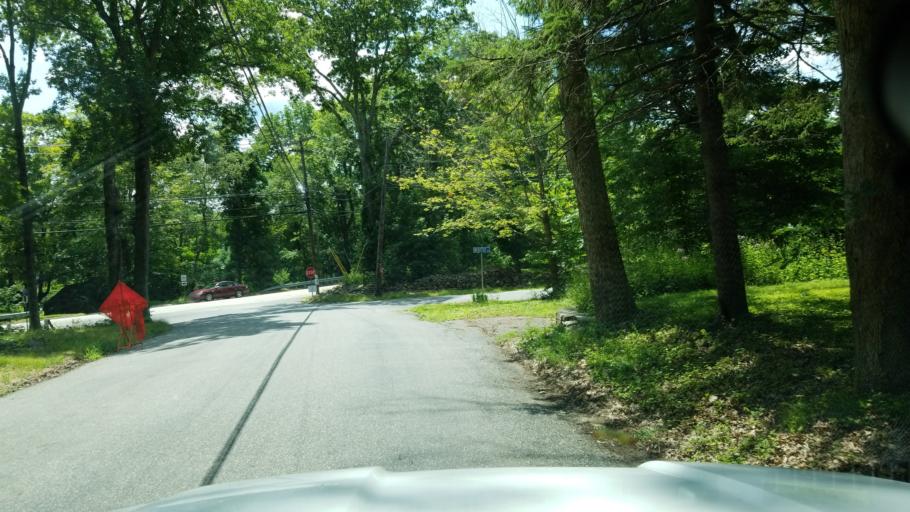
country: US
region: Massachusetts
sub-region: Hampden County
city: Holland
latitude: 41.9737
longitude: -72.1905
